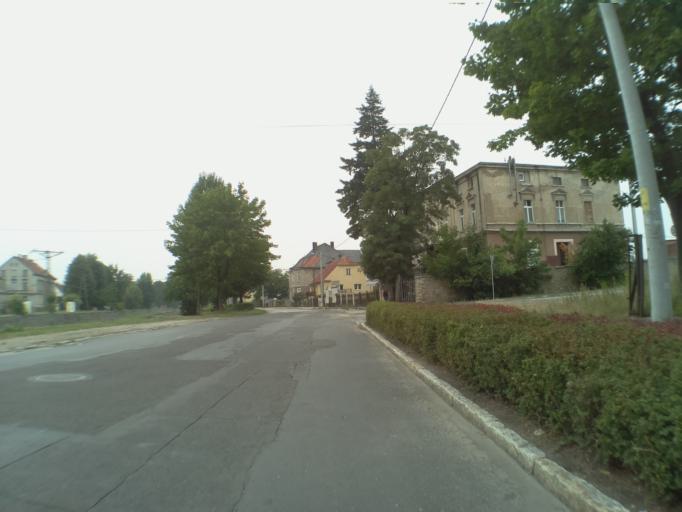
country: PL
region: Lower Silesian Voivodeship
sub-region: Powiat swidnicki
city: Strzegom
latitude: 50.9552
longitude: 16.3414
